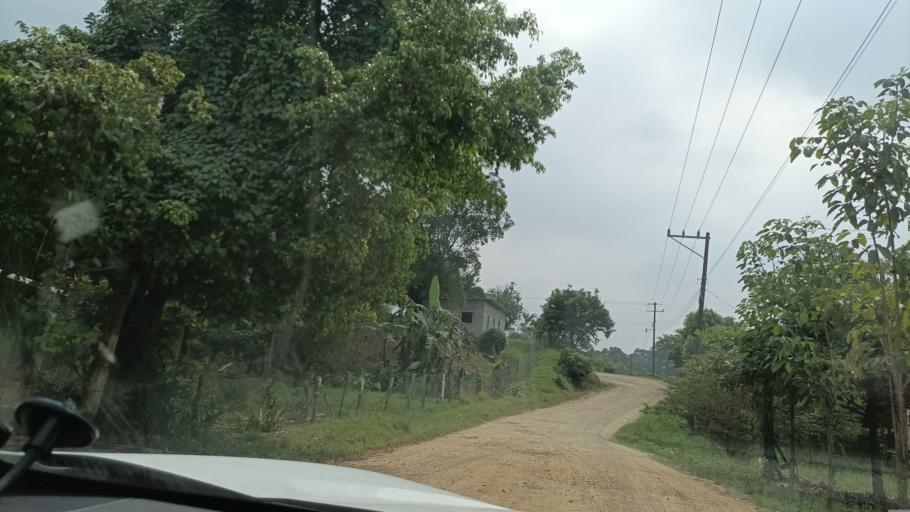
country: MX
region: Veracruz
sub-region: Moloacan
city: Cuichapa
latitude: 17.5807
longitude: -94.2335
